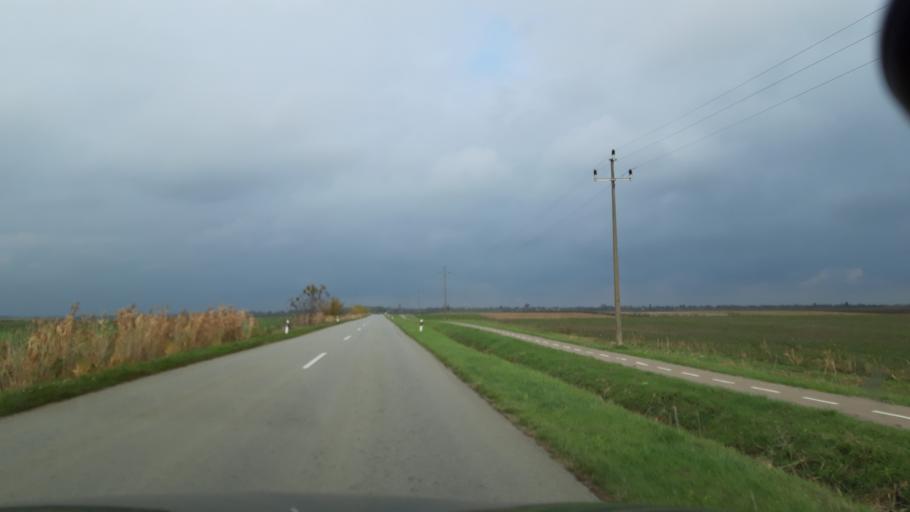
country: HU
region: Csongrad
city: Roszke
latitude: 46.1393
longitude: 20.0963
